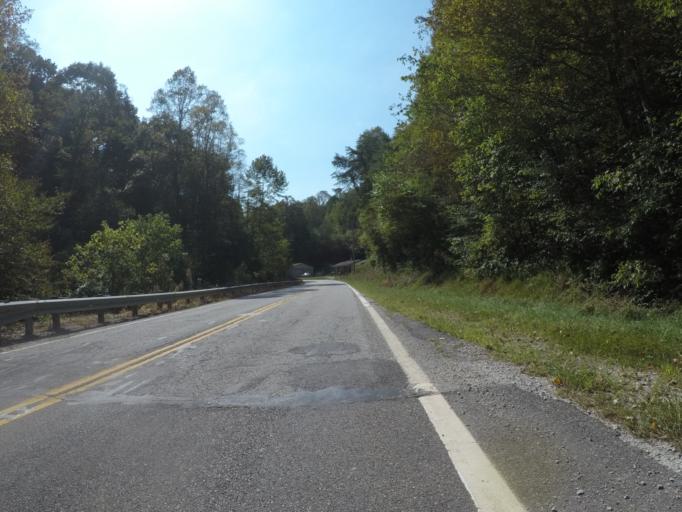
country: US
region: West Virginia
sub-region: Cabell County
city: Lesage
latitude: 38.5950
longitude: -82.4318
